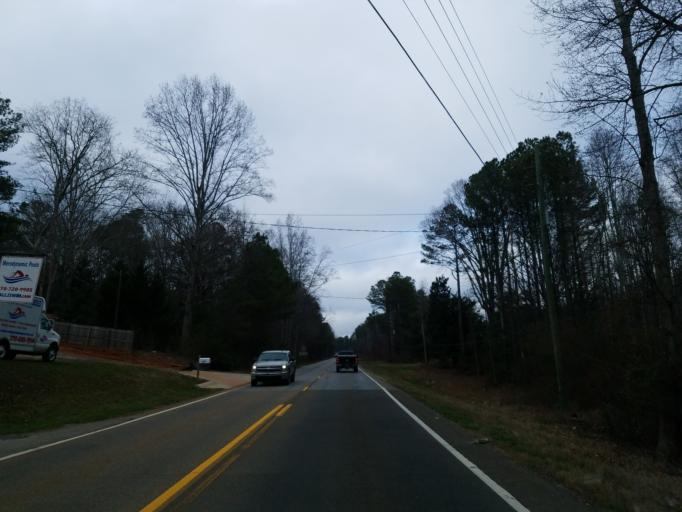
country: US
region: Georgia
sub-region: Cherokee County
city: Canton
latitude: 34.2775
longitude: -84.5079
